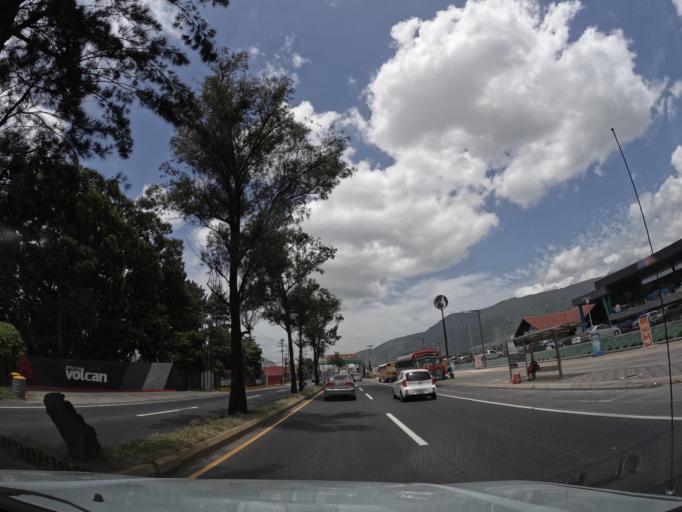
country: GT
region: Guatemala
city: Amatitlan
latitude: 14.4847
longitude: -90.6279
